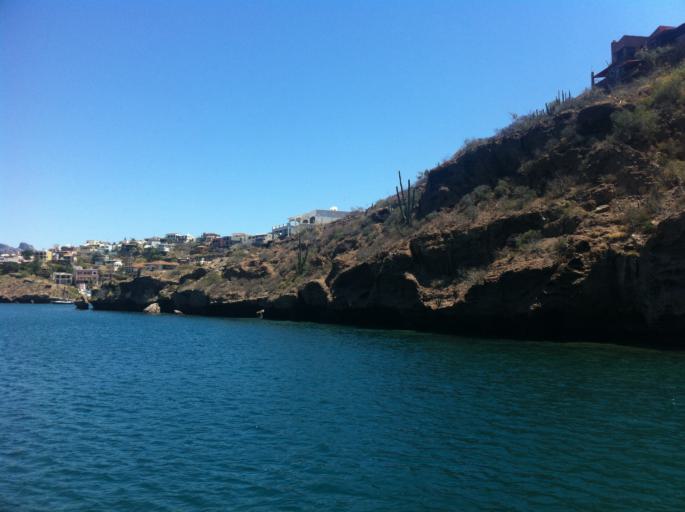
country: MX
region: Sonora
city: Heroica Guaymas
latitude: 27.9393
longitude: -111.0589
